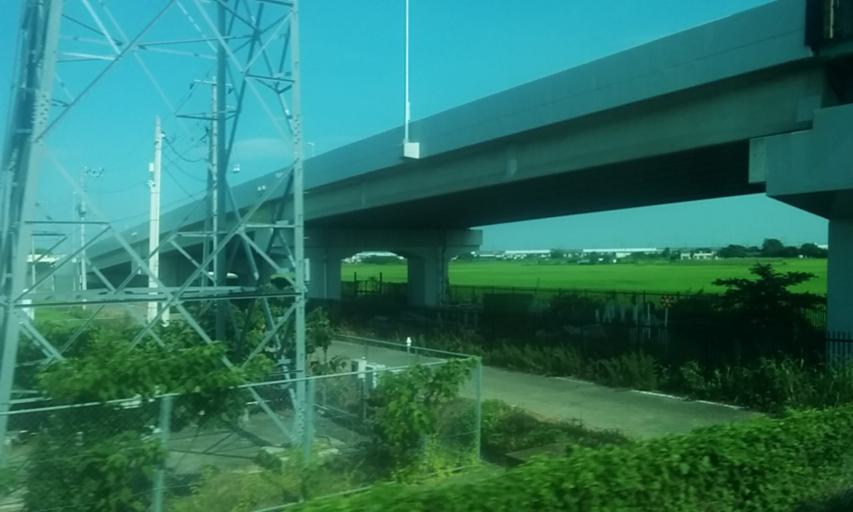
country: JP
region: Saitama
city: Shiraoka
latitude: 36.0241
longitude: 139.6673
